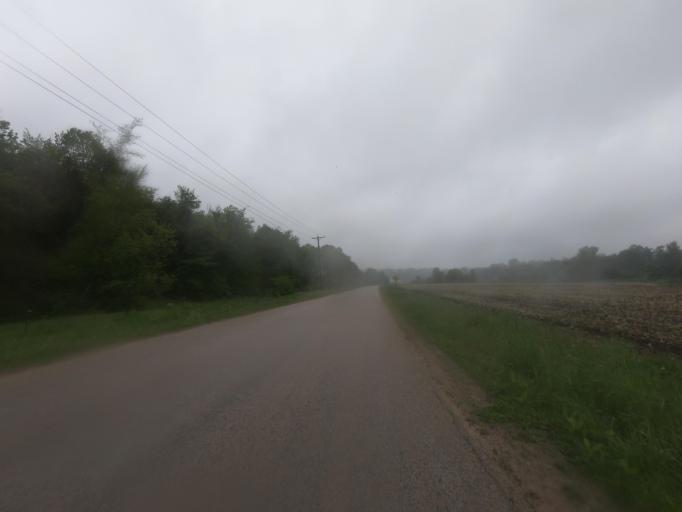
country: US
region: Wisconsin
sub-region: Grant County
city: Hazel Green
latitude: 42.5076
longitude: -90.4766
